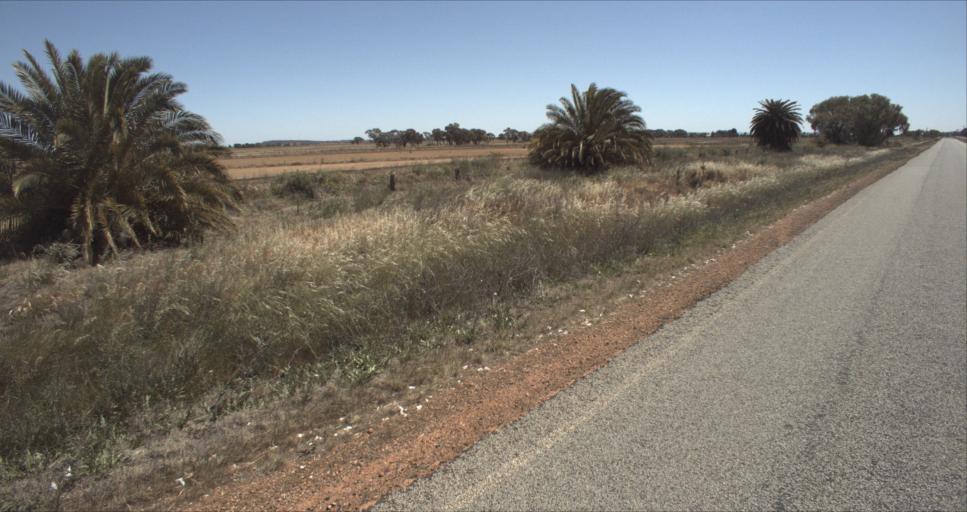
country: AU
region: New South Wales
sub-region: Leeton
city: Leeton
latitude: -34.4503
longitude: 146.2961
